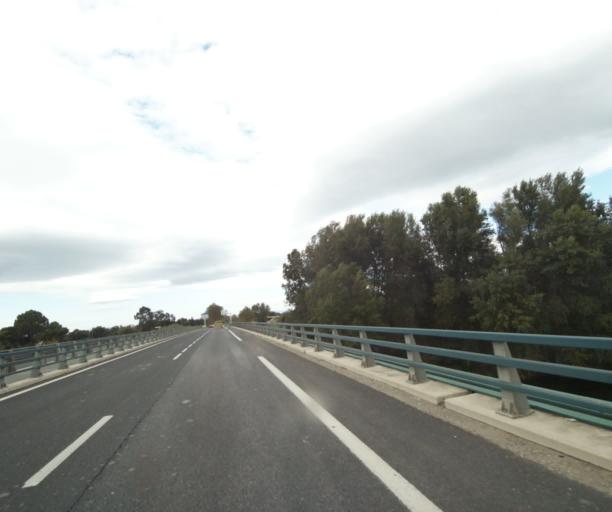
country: FR
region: Languedoc-Roussillon
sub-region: Departement des Pyrenees-Orientales
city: Elne
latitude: 42.5853
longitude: 2.9855
